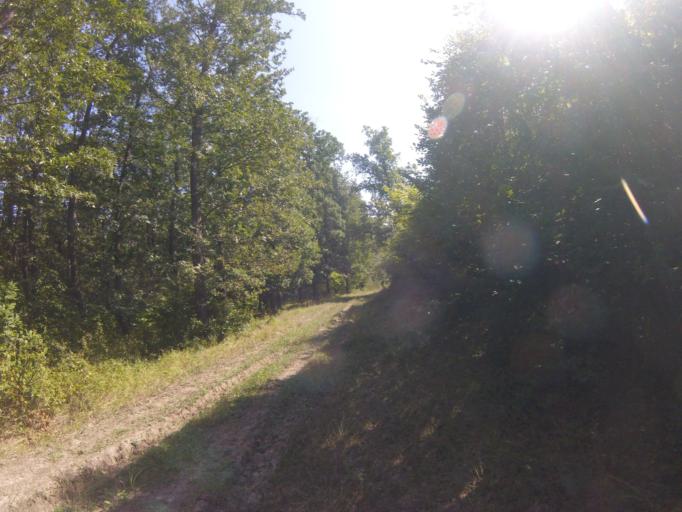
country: HU
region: Nograd
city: Bujak
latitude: 47.8971
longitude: 19.5124
